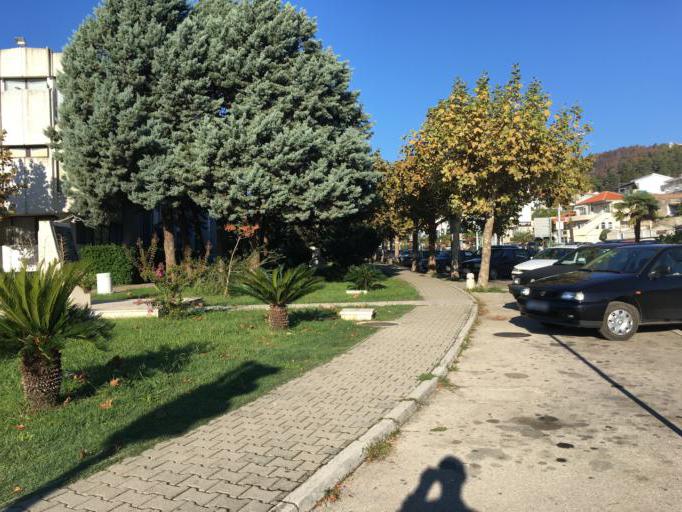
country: ME
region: Ulcinj
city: Ulcinj
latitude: 41.9294
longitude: 19.2182
